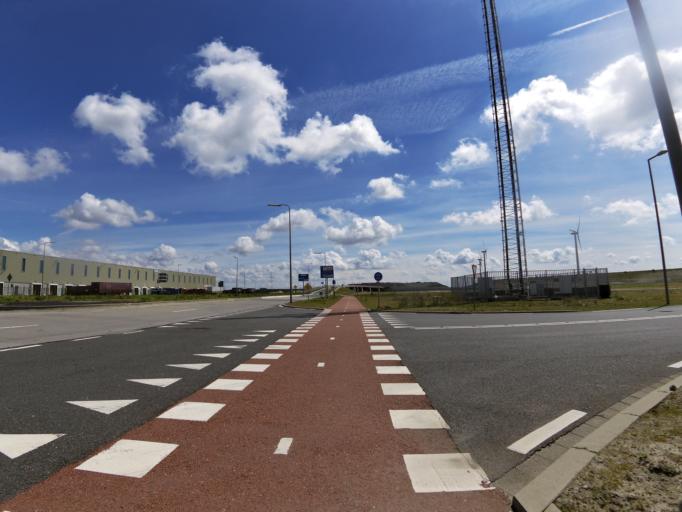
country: NL
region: South Holland
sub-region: Gemeente Rotterdam
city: Hoek van Holland
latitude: 51.9376
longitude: 4.0170
